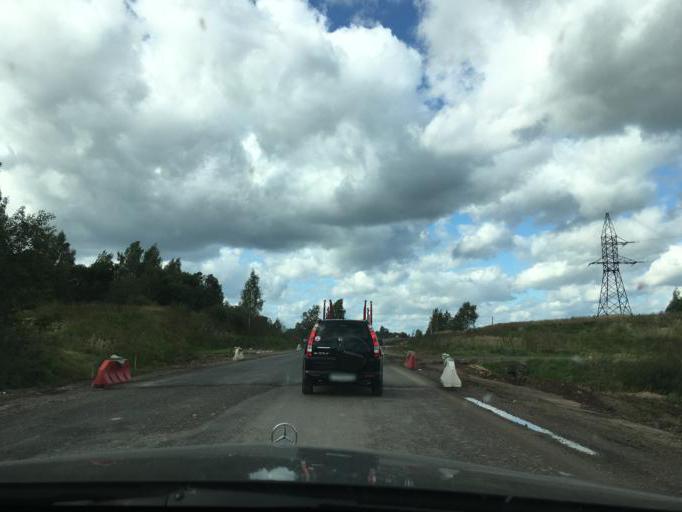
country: RU
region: Pskov
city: Novosokol'niki
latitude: 56.2856
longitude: 30.2617
